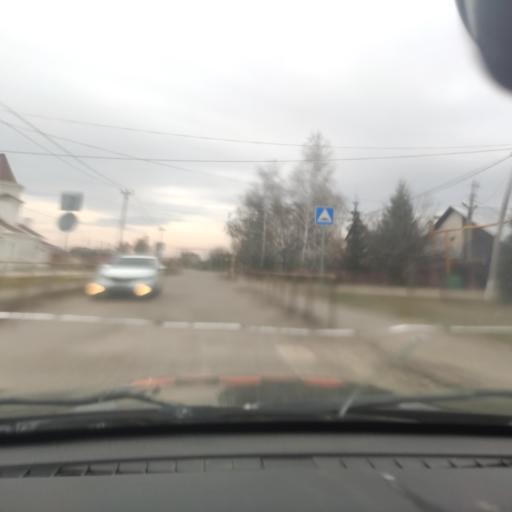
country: RU
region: Samara
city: Podstepki
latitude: 53.5133
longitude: 49.1290
